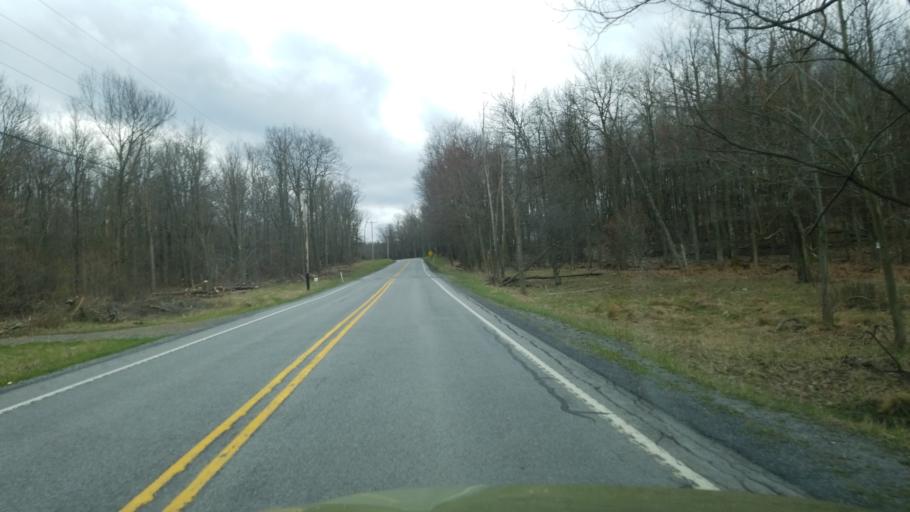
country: US
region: Pennsylvania
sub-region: Blair County
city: Tipton
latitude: 40.7381
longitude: -78.3802
